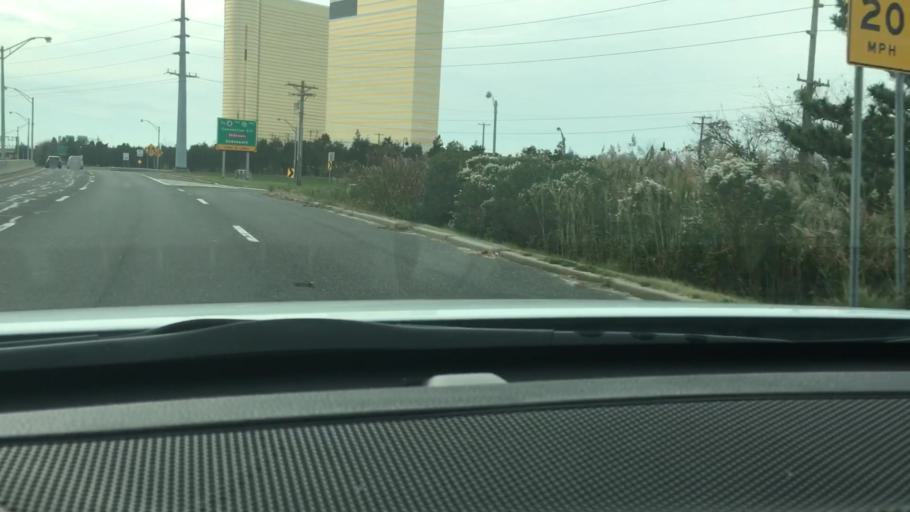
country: US
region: New Jersey
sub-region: Atlantic County
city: Atlantic City
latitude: 39.3817
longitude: -74.4282
